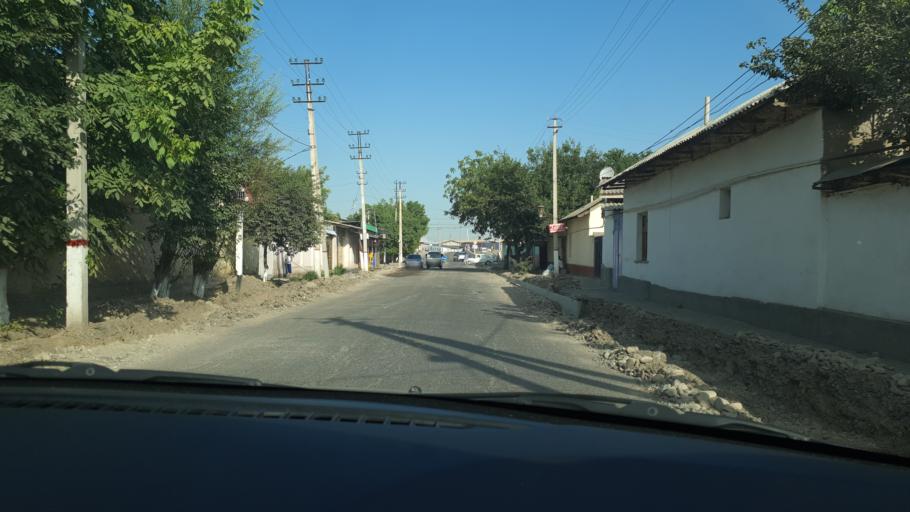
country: UZ
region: Toshkent
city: Urtaowul
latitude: 41.2005
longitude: 69.1575
